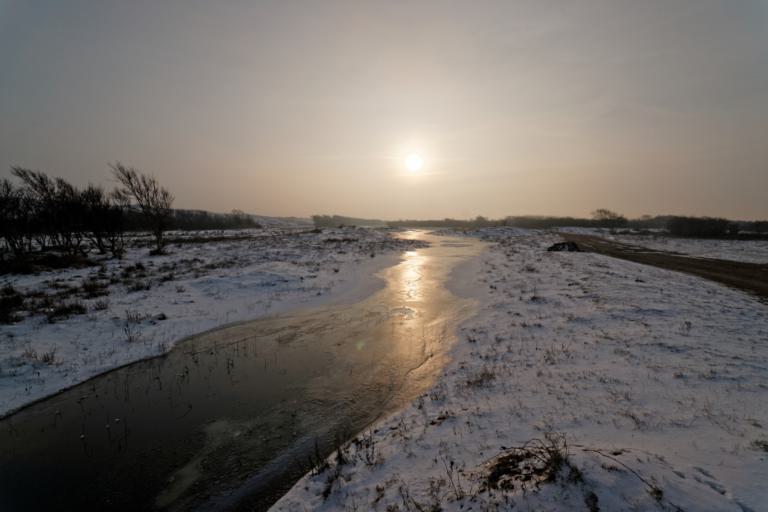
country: NL
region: North Holland
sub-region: Gemeente Texel
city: Den Burg
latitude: 53.1209
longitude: 4.7997
